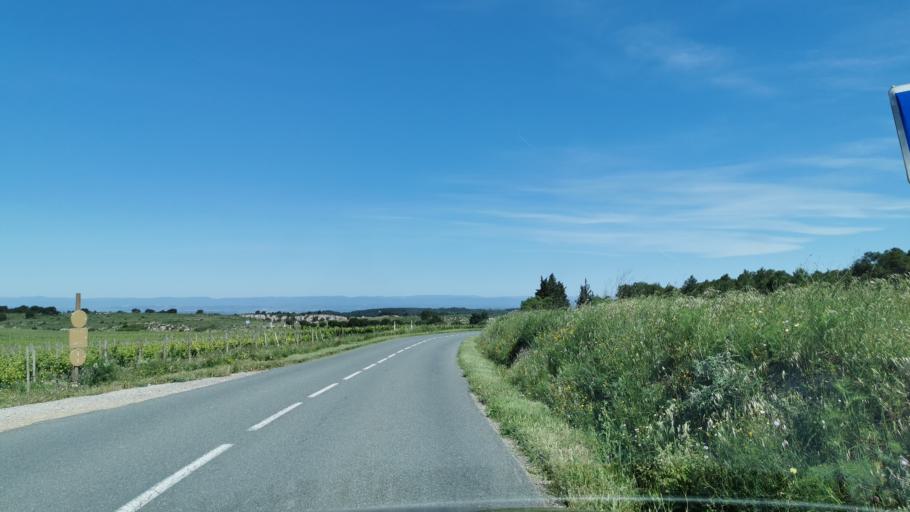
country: FR
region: Languedoc-Roussillon
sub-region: Departement de l'Aude
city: Armissan
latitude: 43.1722
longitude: 3.1124
